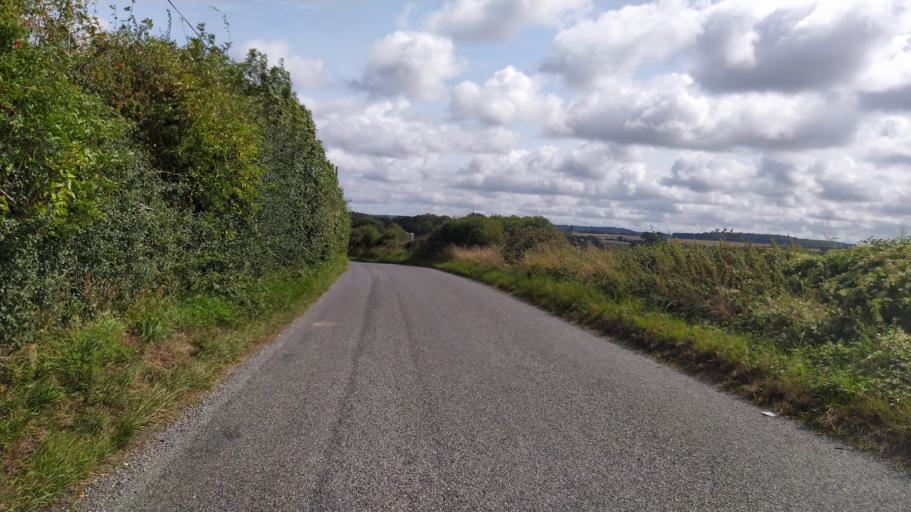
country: GB
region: England
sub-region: Dorset
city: Blandford Forum
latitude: 50.8256
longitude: -2.1135
